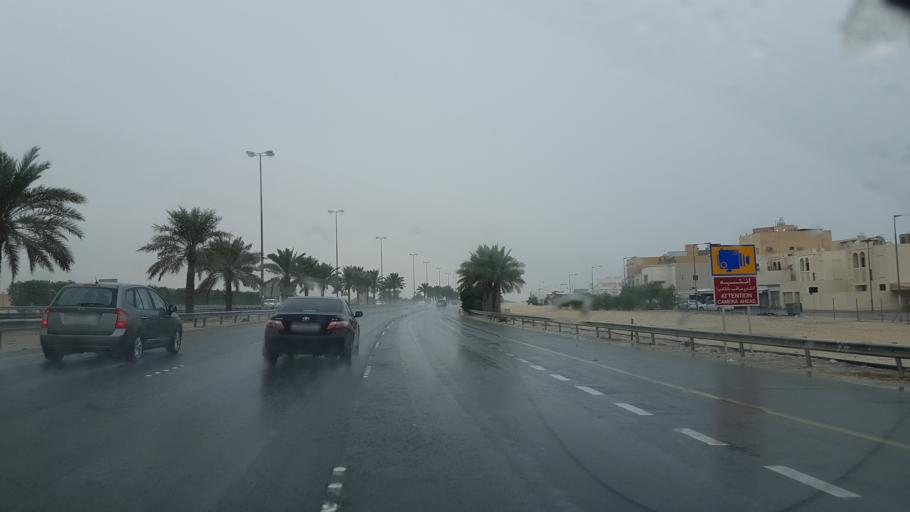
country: BH
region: Central Governorate
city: Madinat Hamad
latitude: 26.1155
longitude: 50.5110
